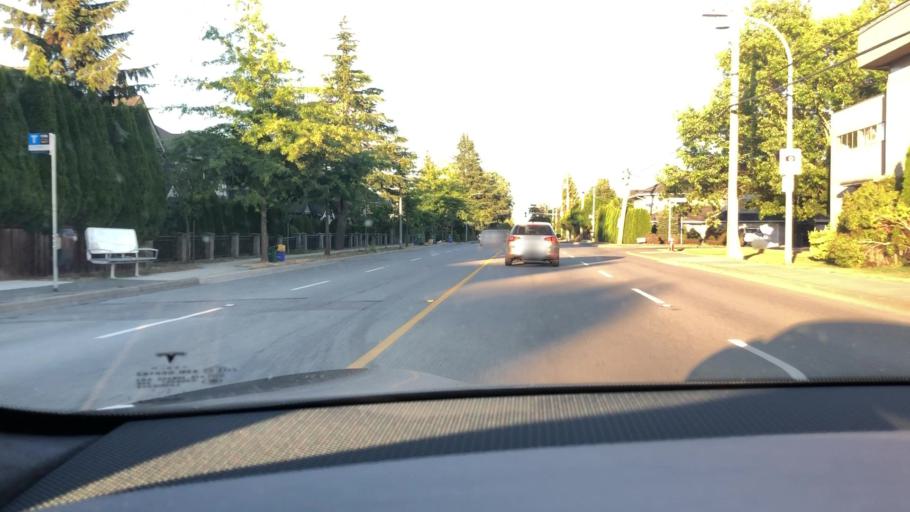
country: CA
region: British Columbia
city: Richmond
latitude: 49.1556
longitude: -123.1508
